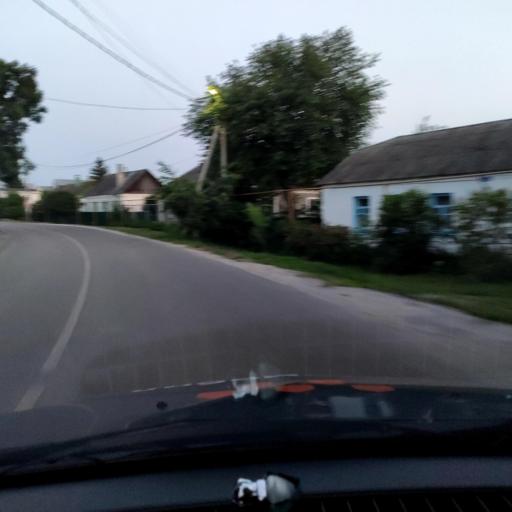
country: RU
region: Voronezj
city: Ramon'
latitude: 51.8202
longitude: 39.2657
